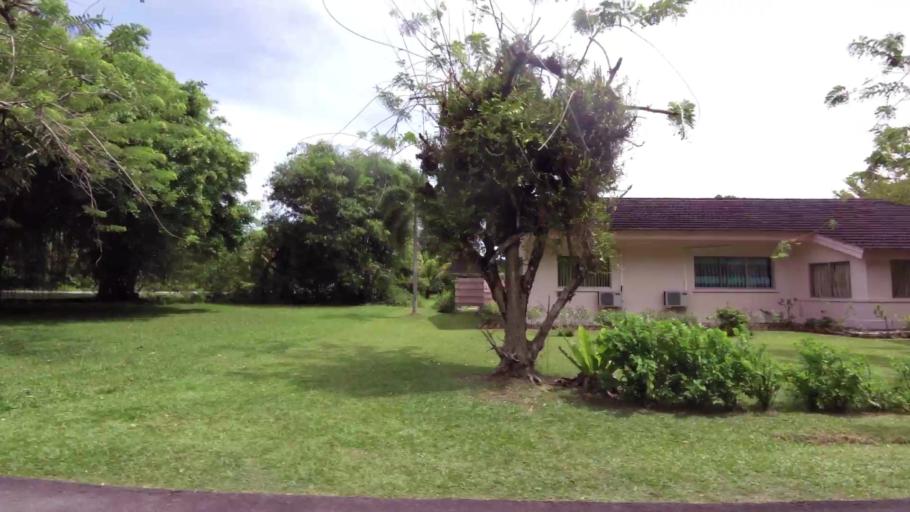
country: BN
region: Belait
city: Seria
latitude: 4.5973
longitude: 114.2875
